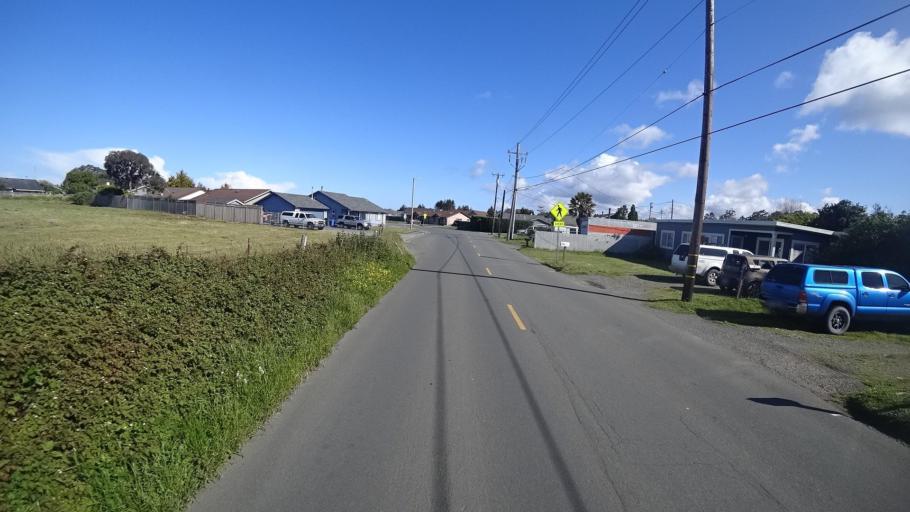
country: US
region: California
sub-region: Humboldt County
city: McKinleyville
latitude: 40.9369
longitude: -124.1077
